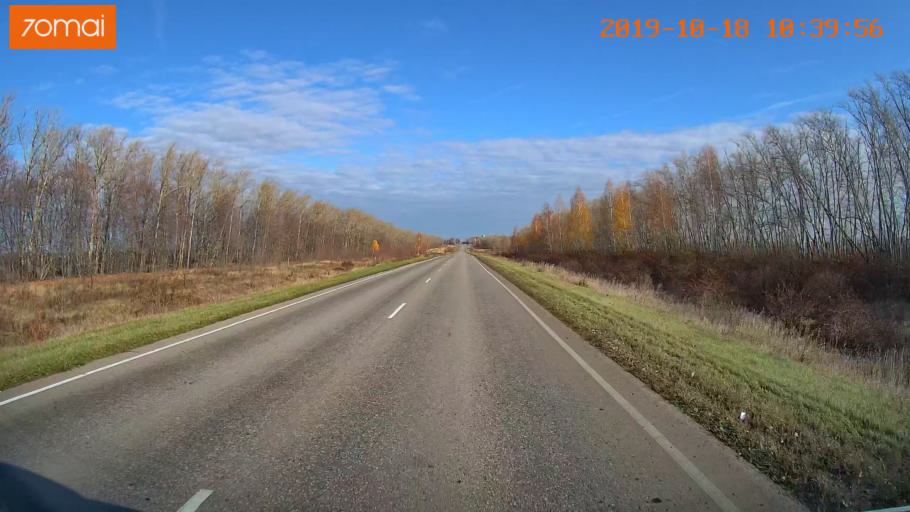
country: RU
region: Tula
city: Kurkino
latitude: 53.5939
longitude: 38.6584
